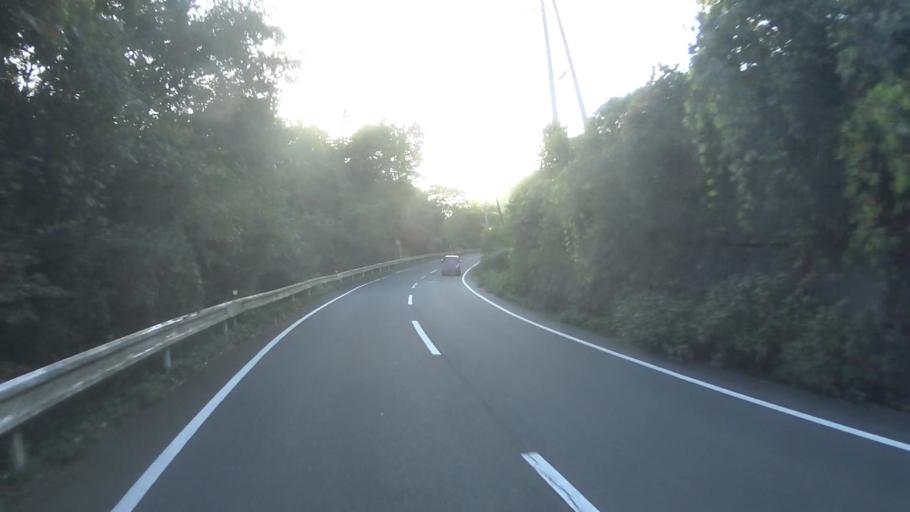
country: JP
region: Kyoto
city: Ayabe
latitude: 35.2249
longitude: 135.2365
